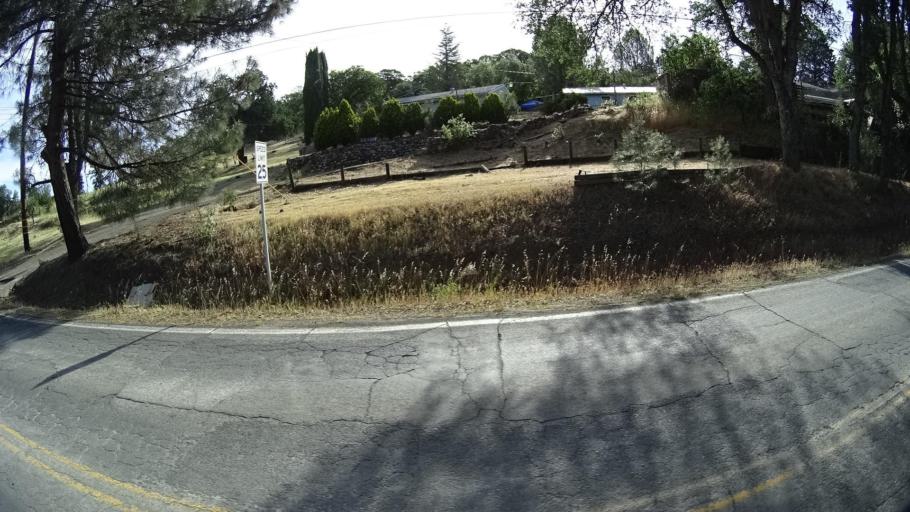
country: US
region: California
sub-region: Lake County
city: Kelseyville
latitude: 38.9728
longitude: -122.8304
